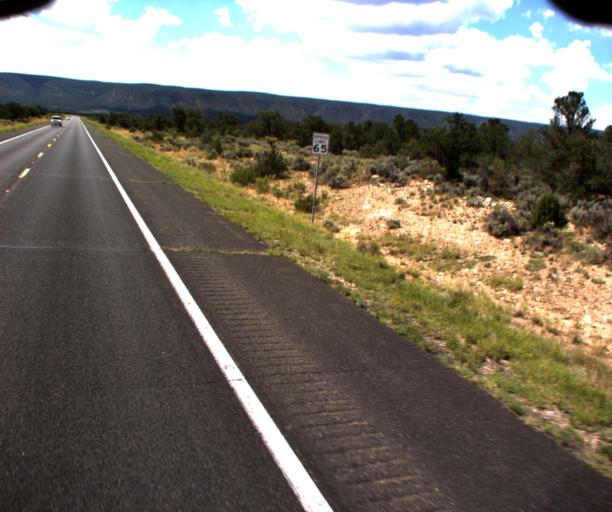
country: US
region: Arizona
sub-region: Coconino County
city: Grand Canyon
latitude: 35.9569
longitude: -111.7832
